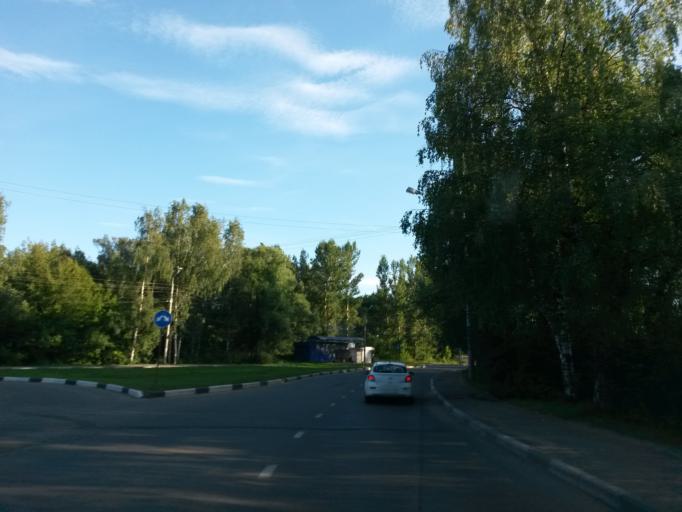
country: RU
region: Jaroslavl
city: Yaroslavl
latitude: 57.6466
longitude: 39.9093
